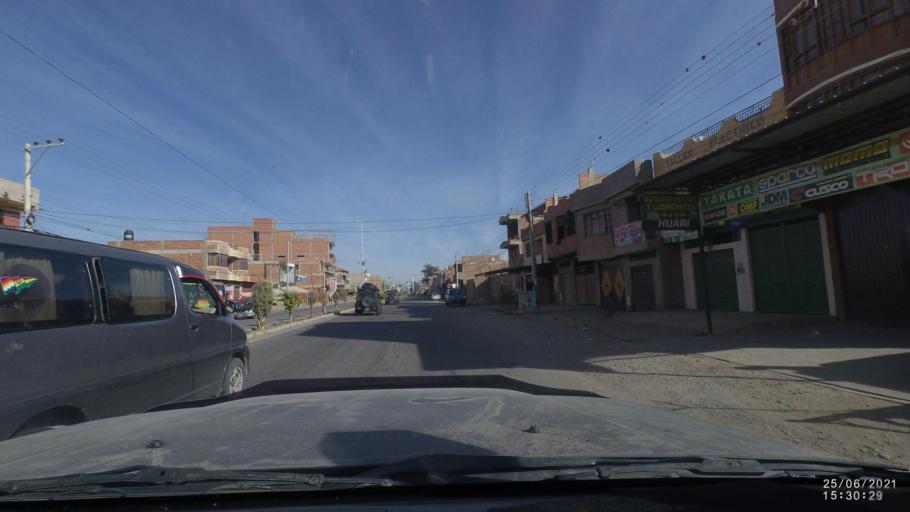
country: BO
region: Cochabamba
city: Cliza
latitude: -17.5848
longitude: -65.9336
